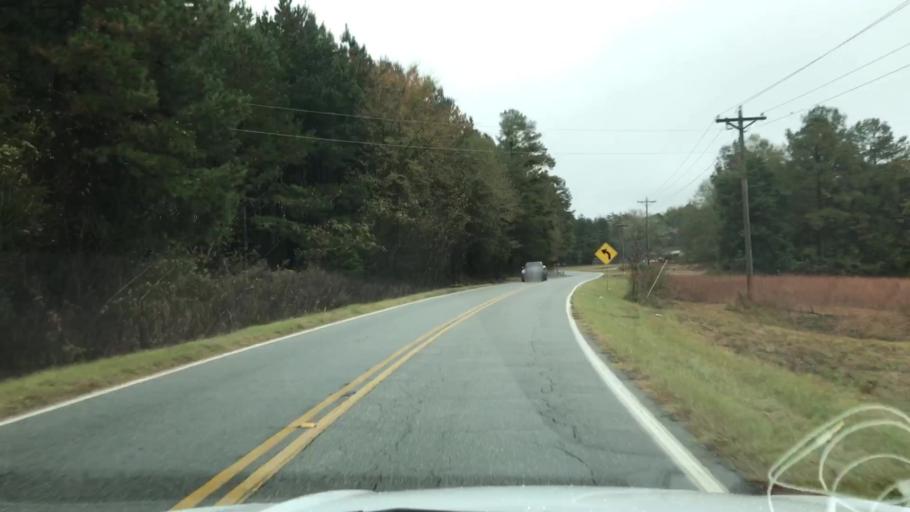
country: US
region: South Carolina
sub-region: Spartanburg County
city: Woodruff
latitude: 34.7474
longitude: -81.9434
